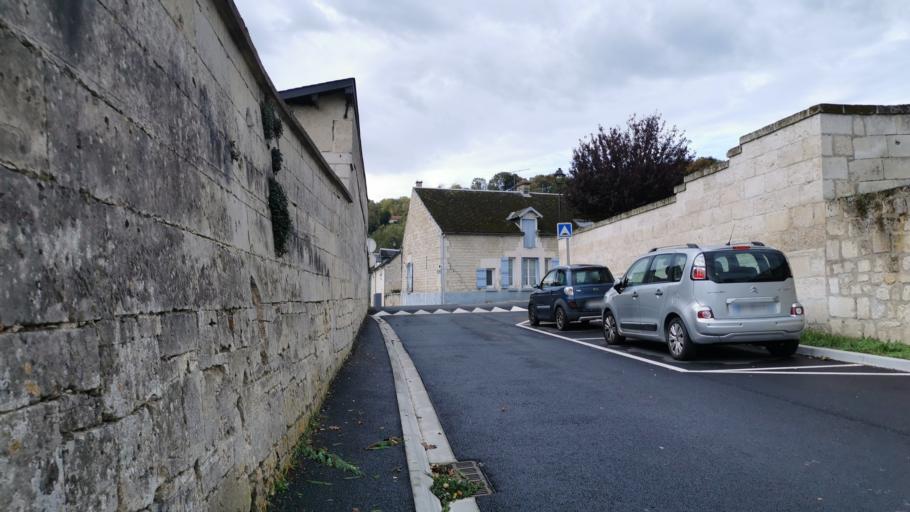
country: FR
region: Picardie
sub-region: Departement de l'Aisne
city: Billy-sur-Aisne
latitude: 49.3536
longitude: 3.3856
